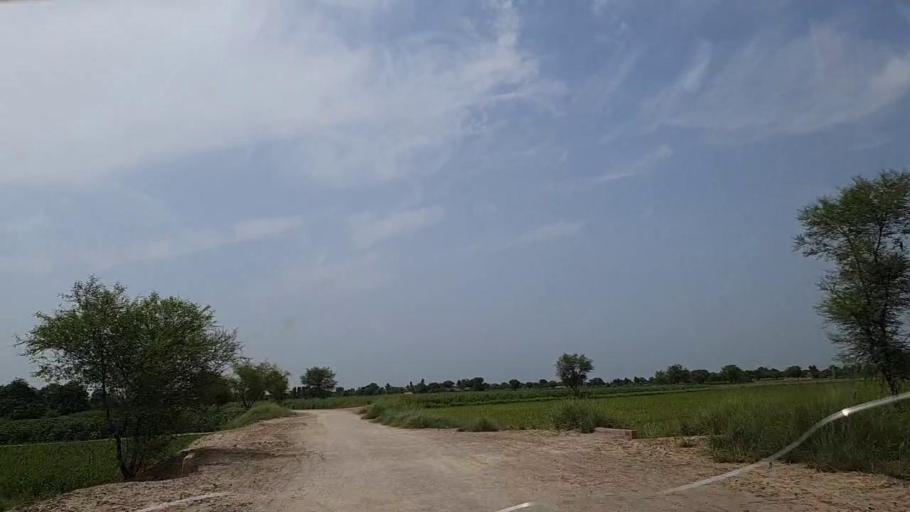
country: PK
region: Sindh
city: Tharu Shah
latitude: 26.8968
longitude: 68.0776
